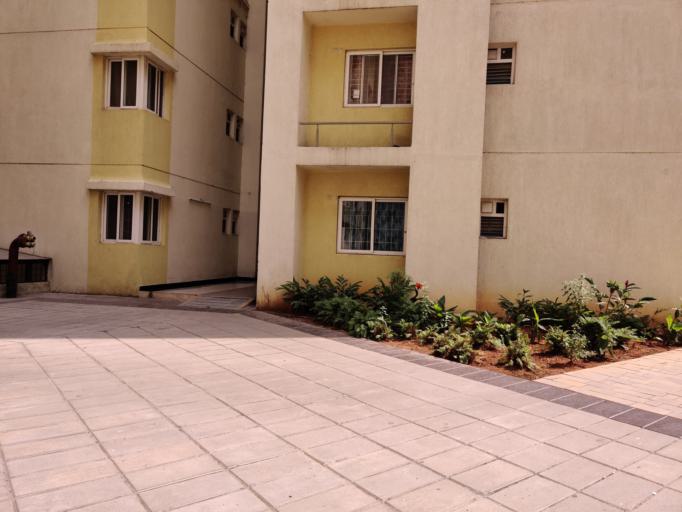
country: IN
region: Telangana
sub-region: Medak
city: Serilingampalle
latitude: 17.4233
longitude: 78.3405
